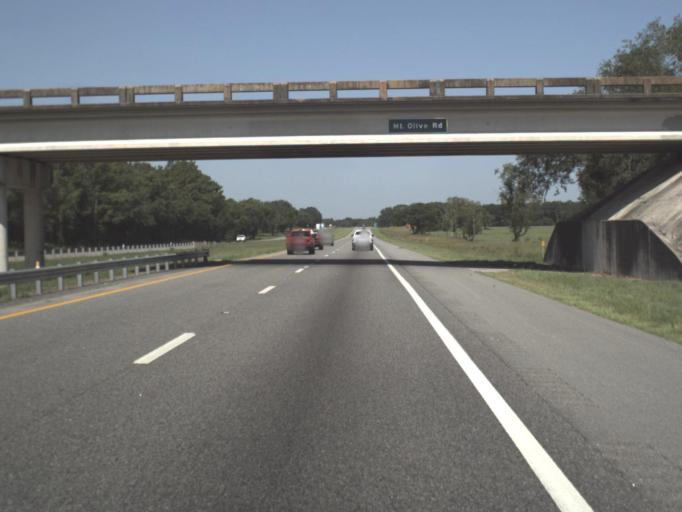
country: US
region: Florida
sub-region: Suwannee County
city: Live Oak
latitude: 30.3493
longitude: -83.0640
